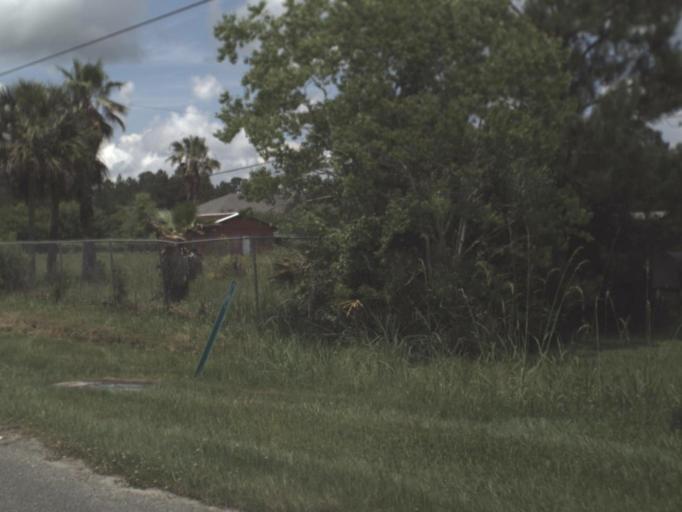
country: US
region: Florida
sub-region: Nassau County
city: Yulee
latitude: 30.6396
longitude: -81.6101
